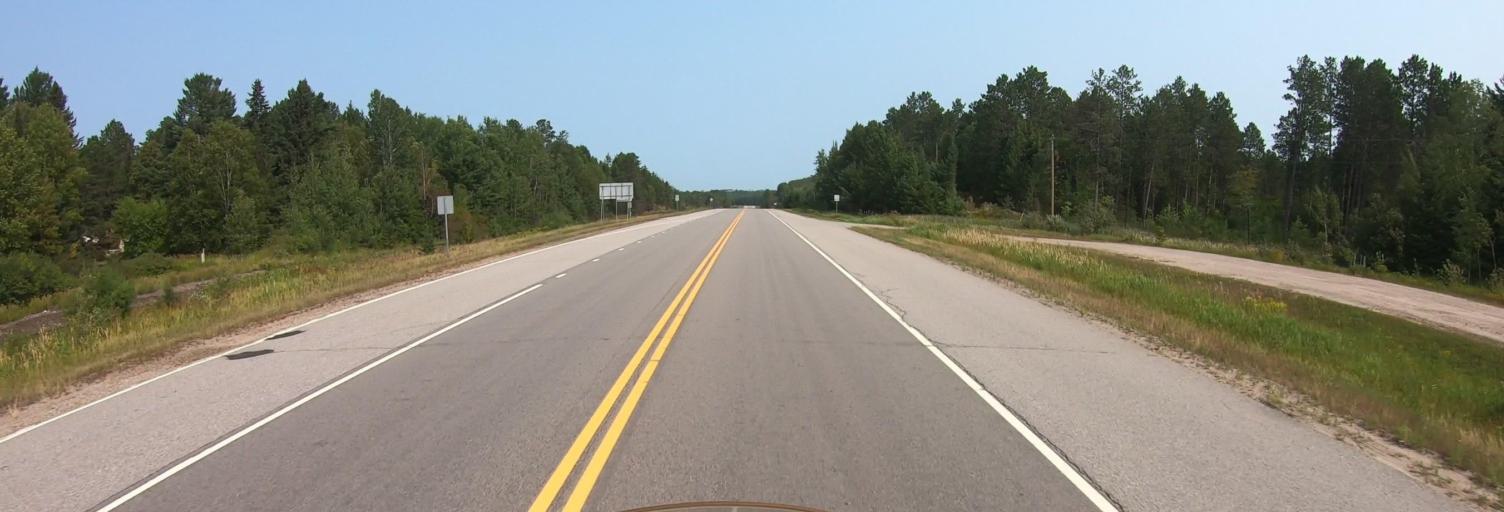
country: US
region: Minnesota
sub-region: Saint Louis County
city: Mountain Iron
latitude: 48.1021
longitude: -92.8434
